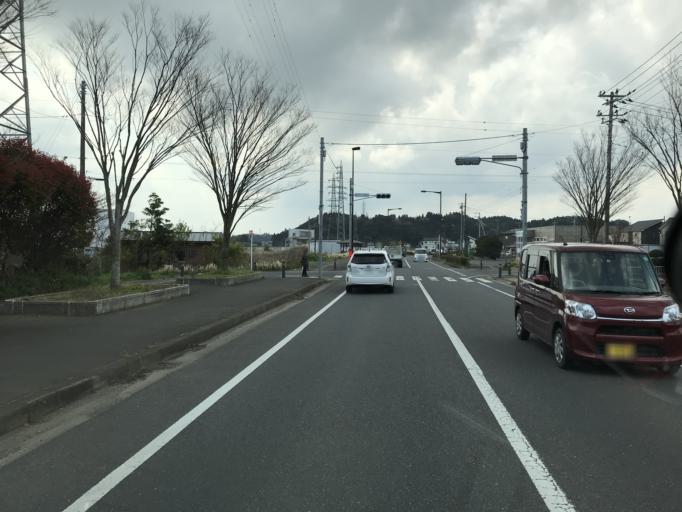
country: JP
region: Chiba
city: Sawara
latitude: 35.8860
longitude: 140.5090
